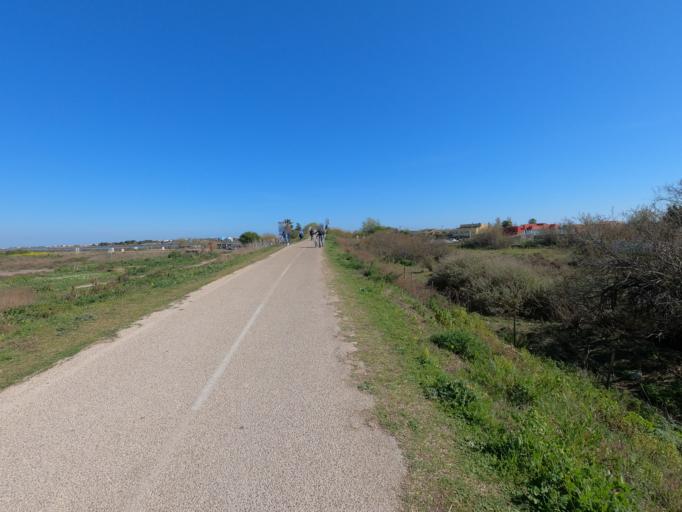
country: FR
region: Languedoc-Roussillon
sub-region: Departement de l'Herault
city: Palavas-les-Flots
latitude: 43.5351
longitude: 3.9177
